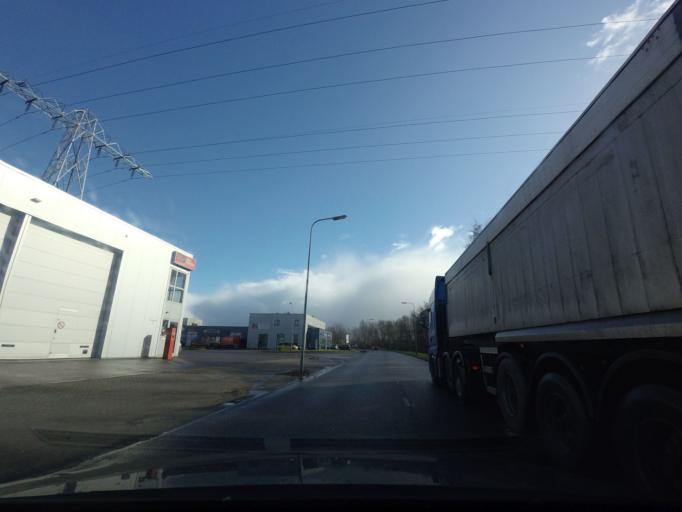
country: NL
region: Groningen
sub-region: Gemeente Groningen
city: Oosterpark
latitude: 53.2138
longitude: 6.6054
